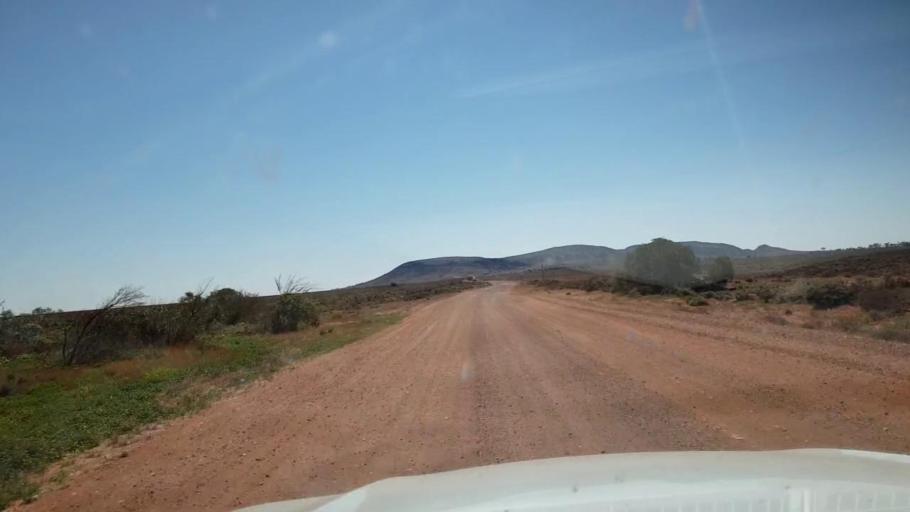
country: AU
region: South Australia
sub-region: Whyalla
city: Whyalla
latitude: -32.7147
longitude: 137.1426
